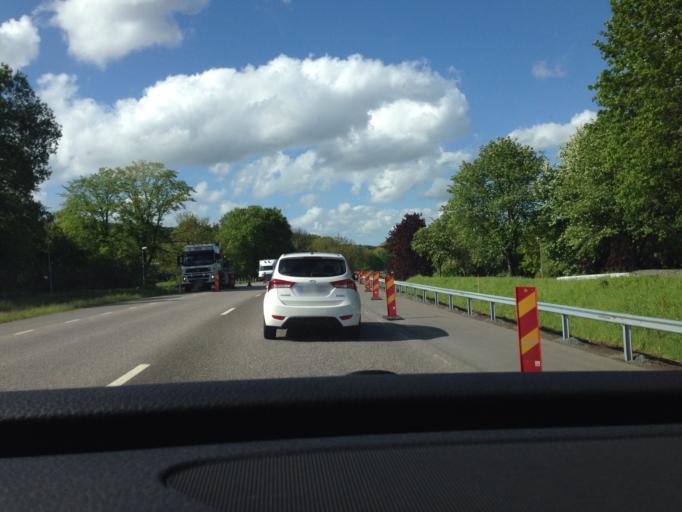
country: SE
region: Vaestra Goetaland
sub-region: Skovde Kommun
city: Skoevde
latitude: 58.3880
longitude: 13.8327
